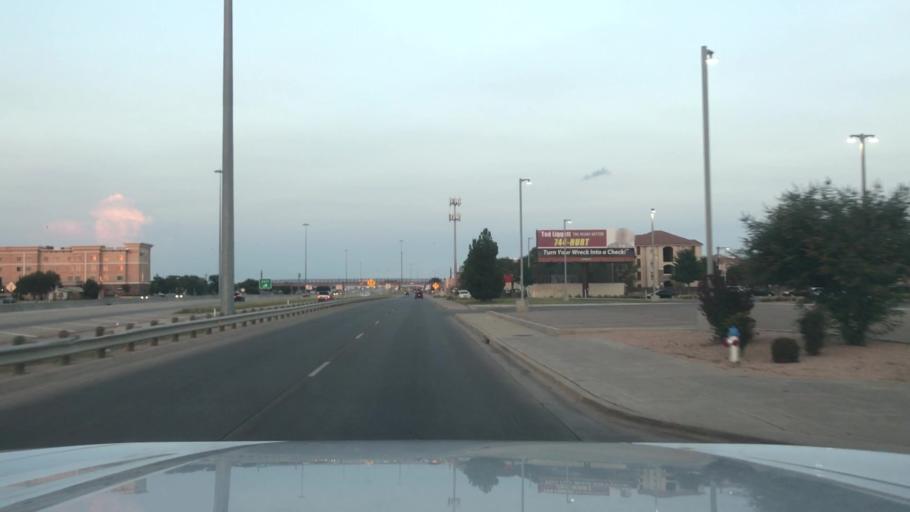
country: US
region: Texas
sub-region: Lubbock County
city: Lubbock
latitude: 33.5923
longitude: -101.8682
